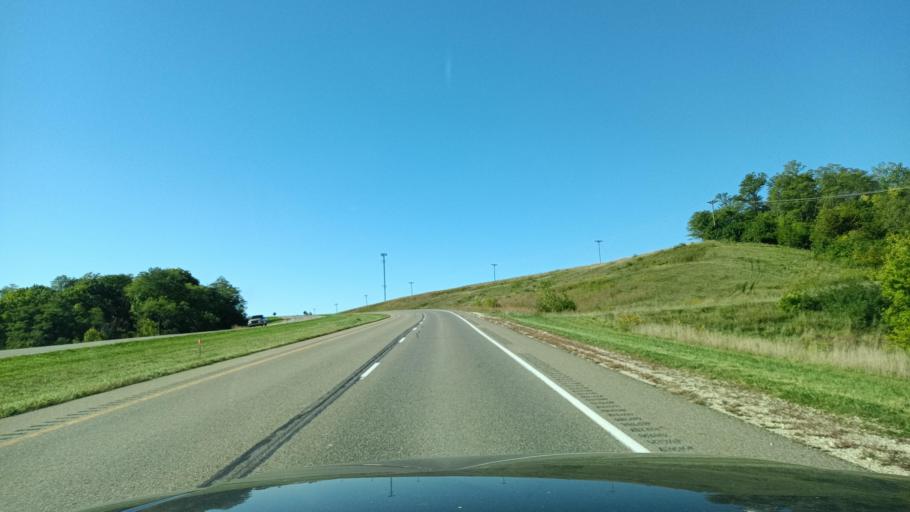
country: US
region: Iowa
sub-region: Lee County
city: Fort Madison
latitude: 40.6924
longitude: -91.2481
